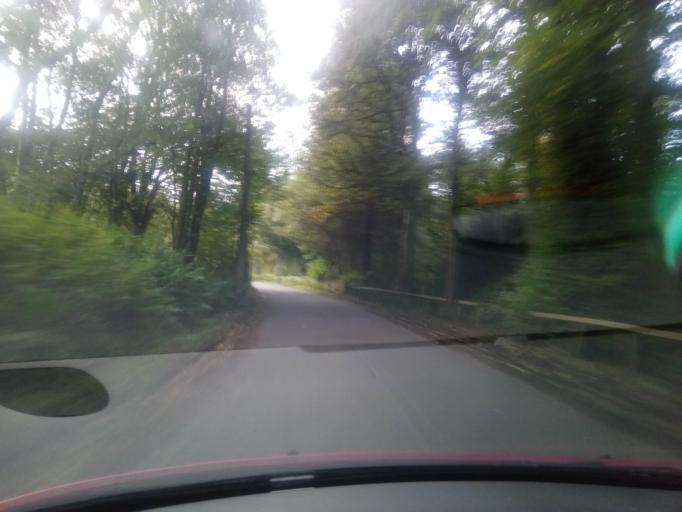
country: GB
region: Scotland
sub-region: The Scottish Borders
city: Jedburgh
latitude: 55.3771
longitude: -2.6474
